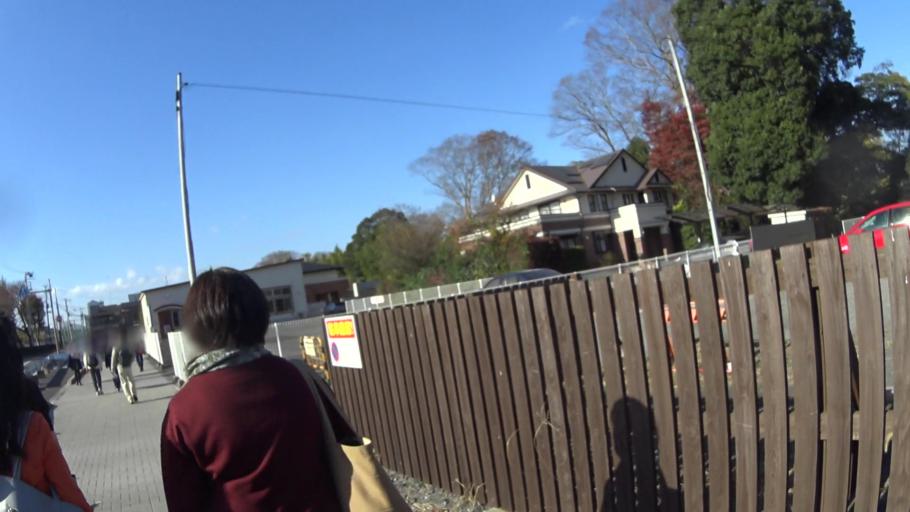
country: JP
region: Ibaraki
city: Mito-shi
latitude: 36.3784
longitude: 140.4744
